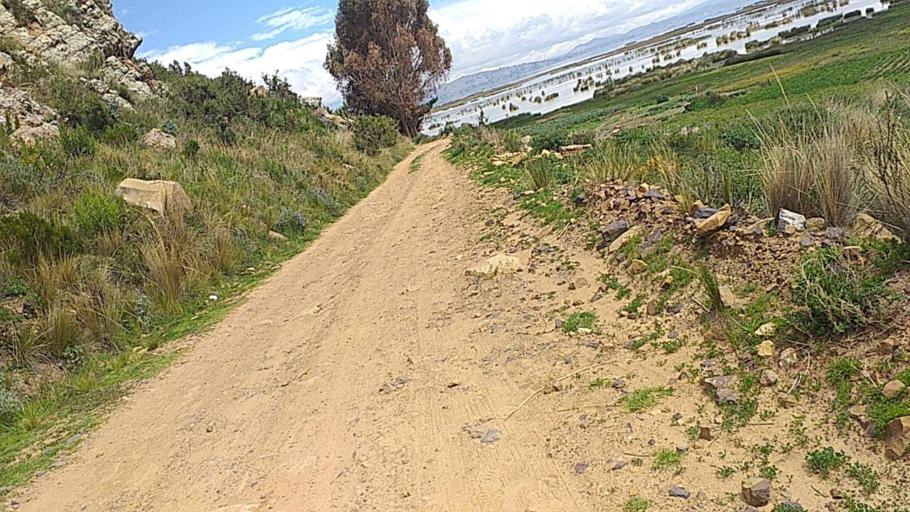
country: BO
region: La Paz
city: Batallas
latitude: -16.3279
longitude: -68.6429
